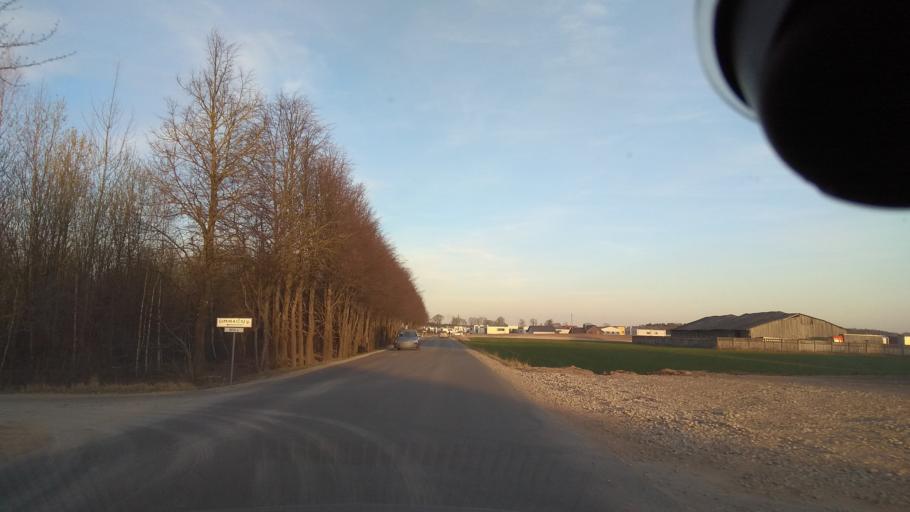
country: LT
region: Vilnius County
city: Pasilaiciai
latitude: 54.7599
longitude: 25.2167
